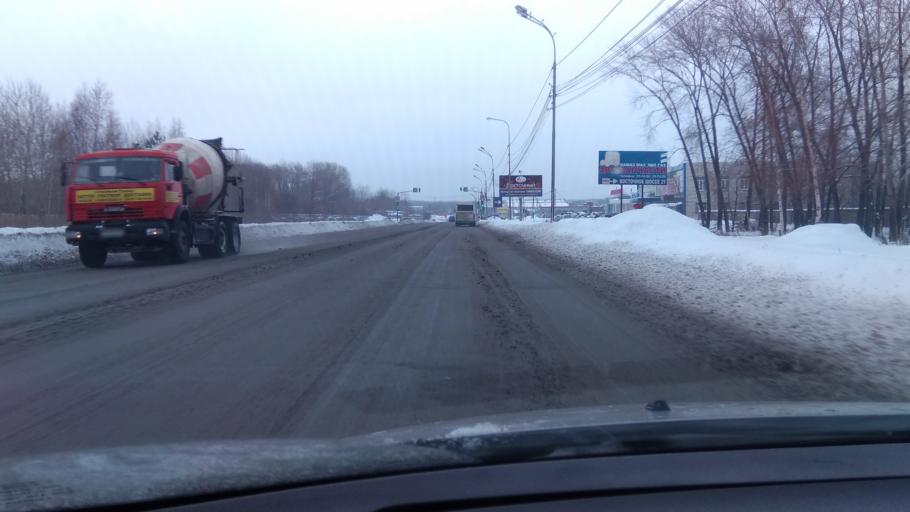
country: RU
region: Sverdlovsk
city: Nizhniy Tagil
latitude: 57.9090
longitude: 60.0195
